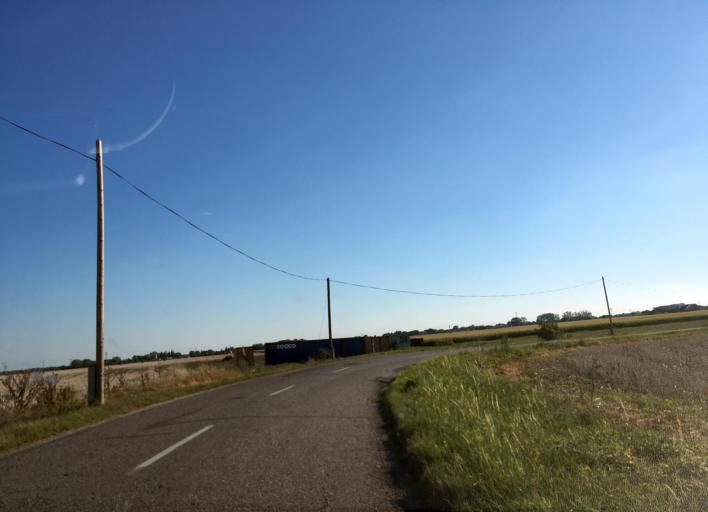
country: SK
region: Trnavsky
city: Samorin
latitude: 48.0303
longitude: 17.3427
